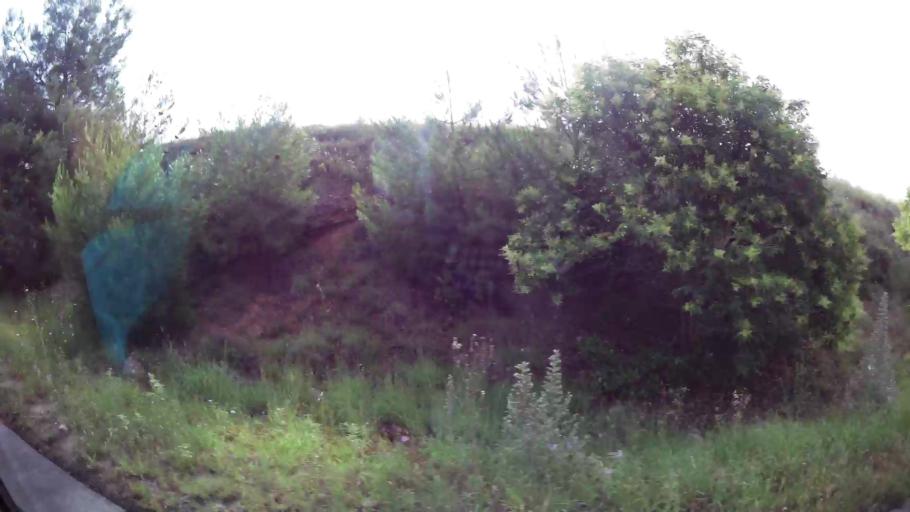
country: GR
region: Central Macedonia
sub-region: Nomos Thessalonikis
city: Panorama
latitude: 40.5689
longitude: 23.0247
